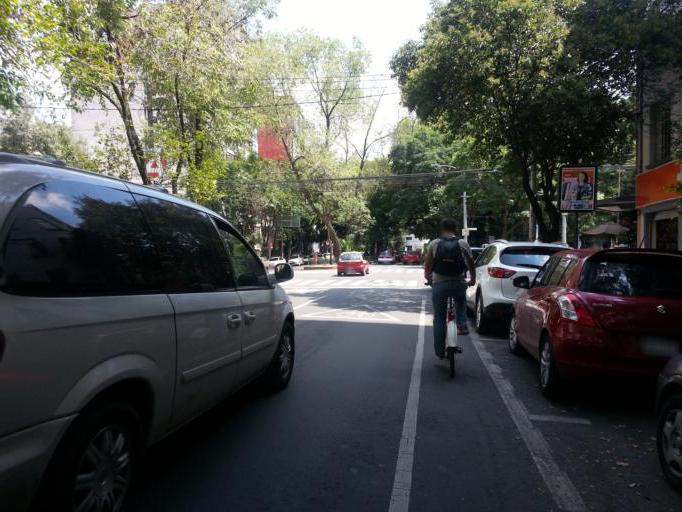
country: MX
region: Mexico City
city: Benito Juarez
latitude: 19.4147
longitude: -99.1693
